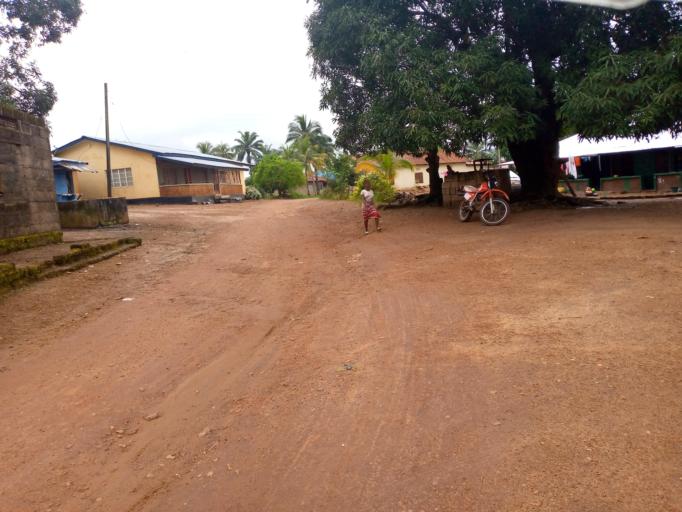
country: SL
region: Eastern Province
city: Kenema
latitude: 7.8676
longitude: -11.1828
